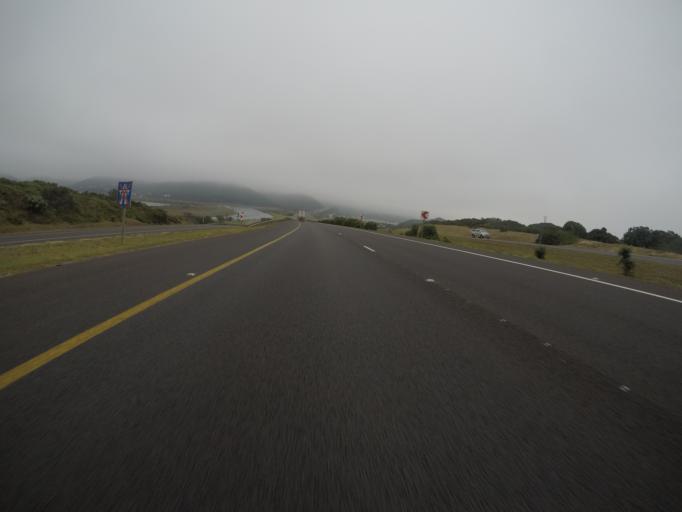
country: ZA
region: Western Cape
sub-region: Eden District Municipality
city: Mossel Bay
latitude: -34.0568
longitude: 22.2184
